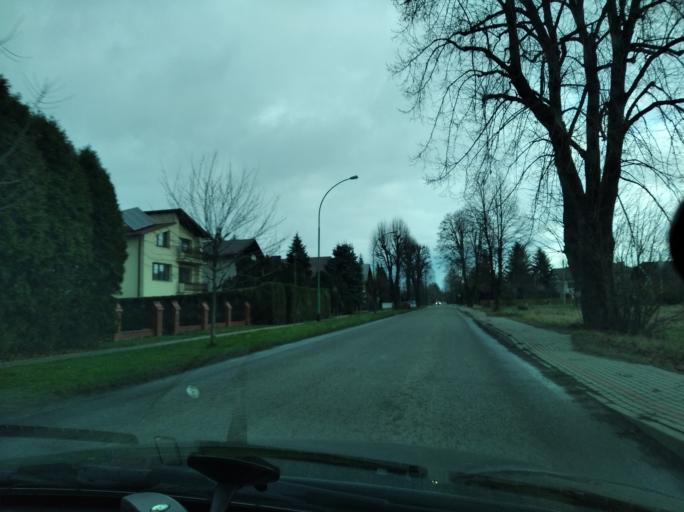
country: PL
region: Subcarpathian Voivodeship
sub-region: Powiat lancucki
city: Lancut
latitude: 50.0902
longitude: 22.2381
